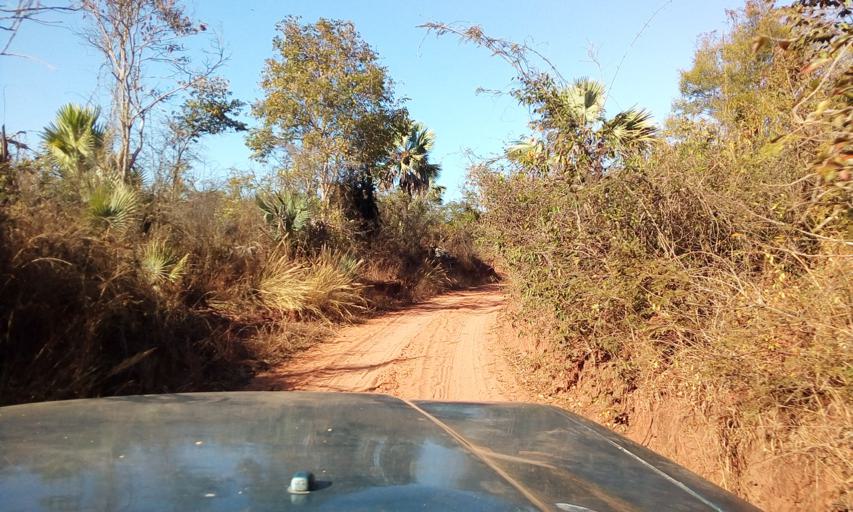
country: MG
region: Boeny
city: Sitampiky
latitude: -16.1917
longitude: 45.3621
